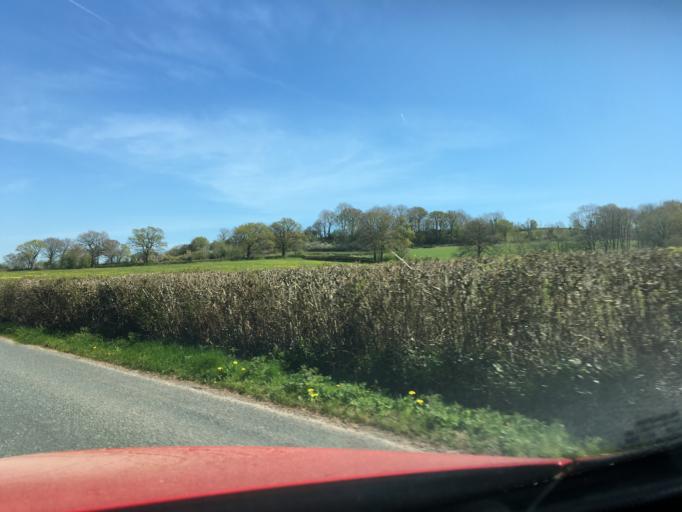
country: GB
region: Wales
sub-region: Monmouthshire
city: Llangwm
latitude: 51.7284
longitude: -2.8295
